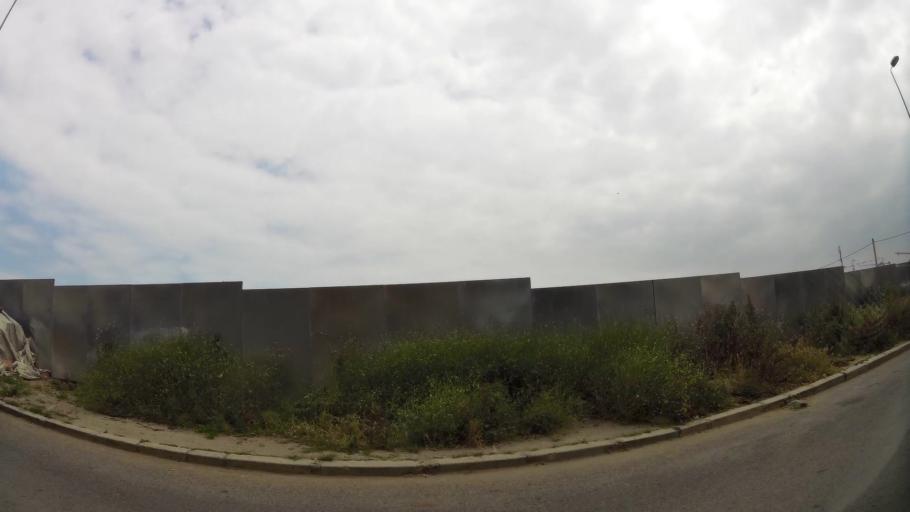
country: MA
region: Rabat-Sale-Zemmour-Zaer
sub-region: Rabat
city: Rabat
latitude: 34.0030
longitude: -6.8633
